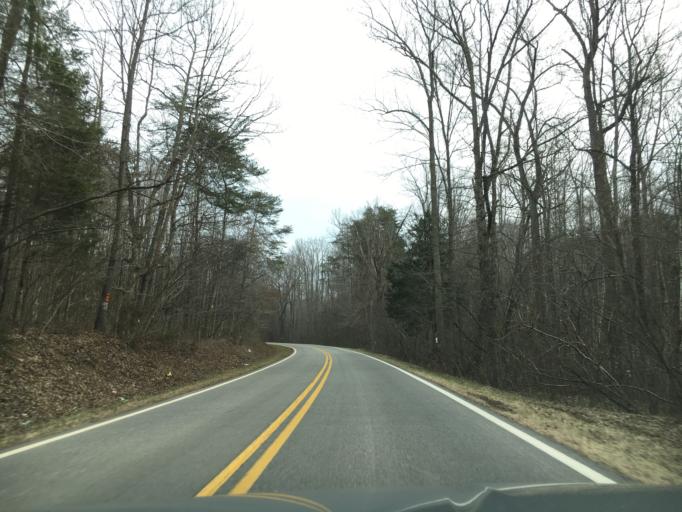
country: US
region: Virginia
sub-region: Charlotte County
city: Charlotte Court House
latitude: 37.1147
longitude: -78.7545
